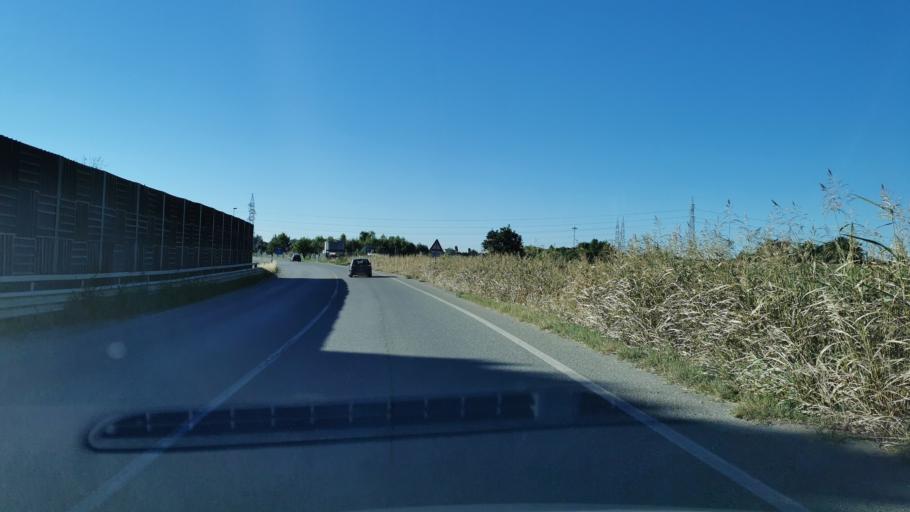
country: IT
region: Piedmont
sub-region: Provincia di Torino
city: Savonera
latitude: 45.1115
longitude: 7.5922
